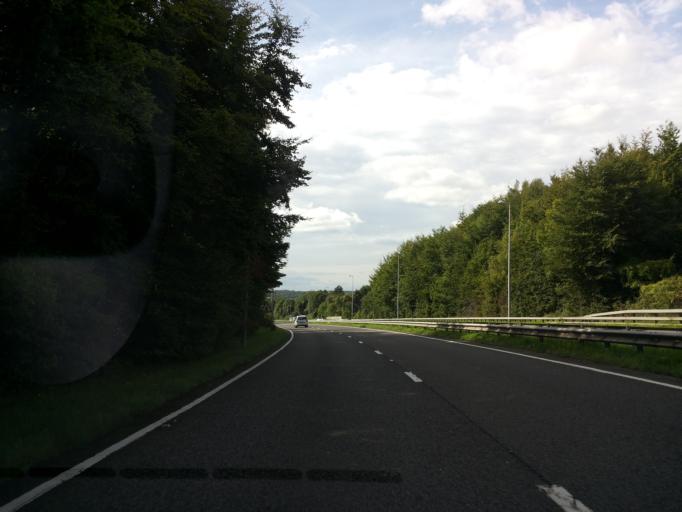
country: GB
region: England
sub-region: Kent
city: Halstead
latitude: 51.3469
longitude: 0.1297
